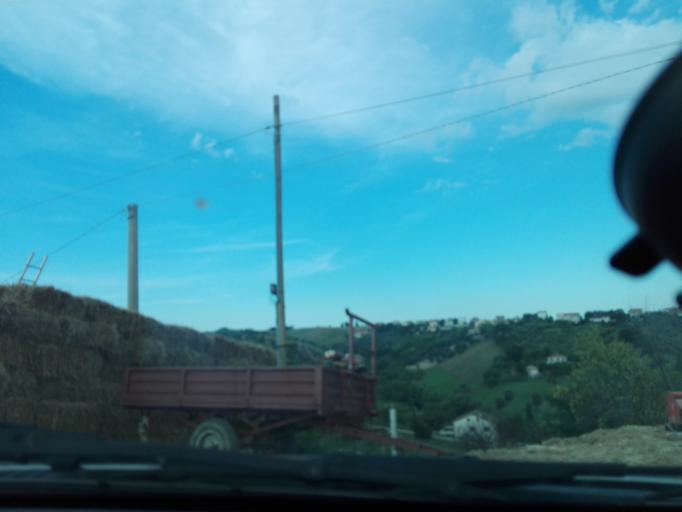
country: IT
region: Abruzzo
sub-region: Provincia di Pescara
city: Cappelle sul Tavo
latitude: 42.4486
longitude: 14.1010
